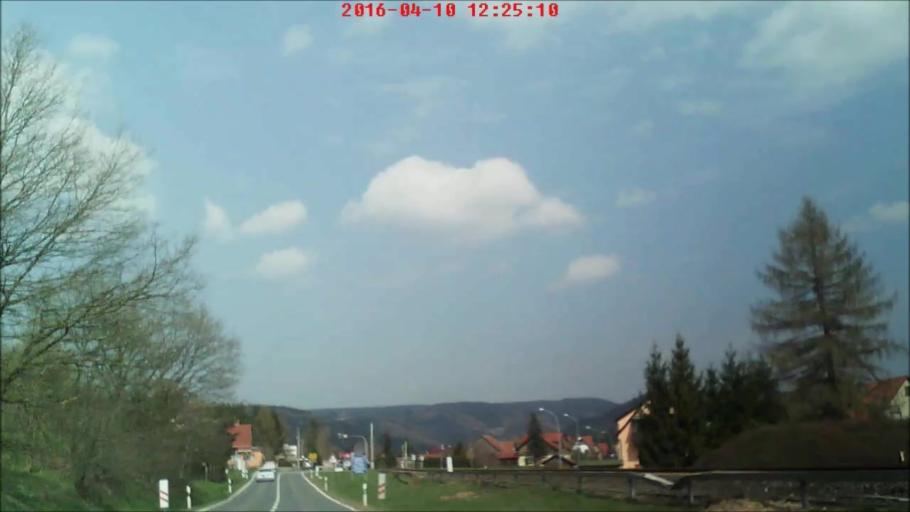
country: DE
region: Thuringia
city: Viernau
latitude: 50.6772
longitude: 10.5523
